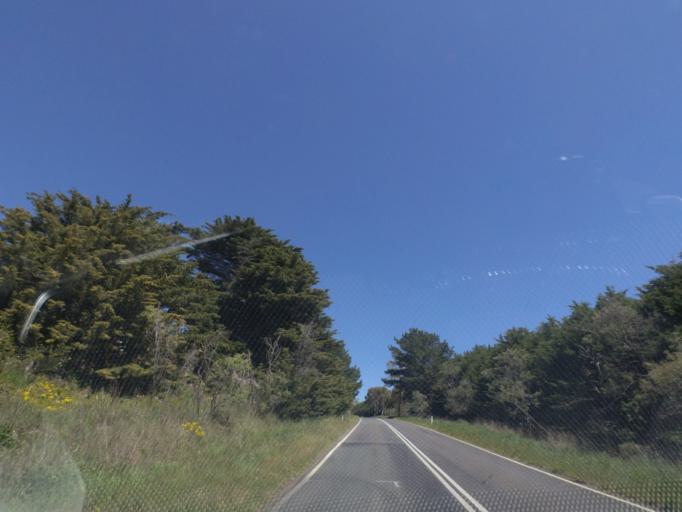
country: AU
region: Victoria
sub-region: Hume
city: Sunbury
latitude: -37.3029
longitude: 144.6850
